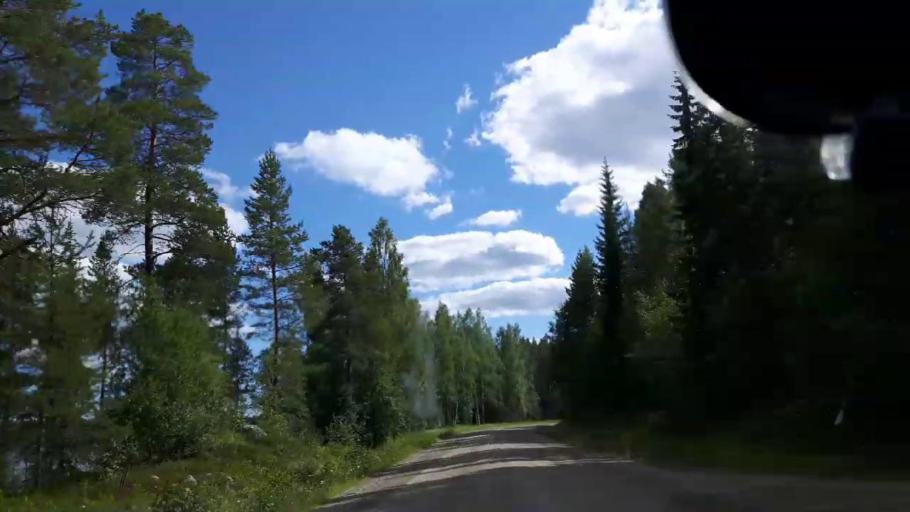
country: SE
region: Vaesternorrland
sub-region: Ange Kommun
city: Ange
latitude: 62.7228
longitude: 15.6372
